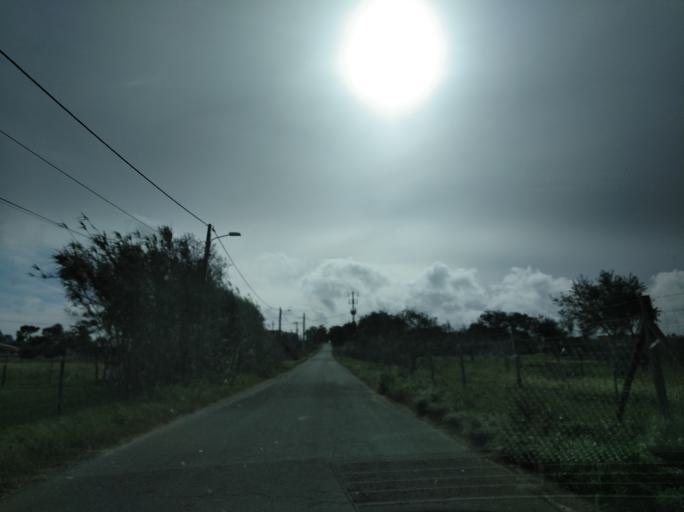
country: PT
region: Setubal
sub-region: Grandola
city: Grandola
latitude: 38.1969
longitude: -8.5481
